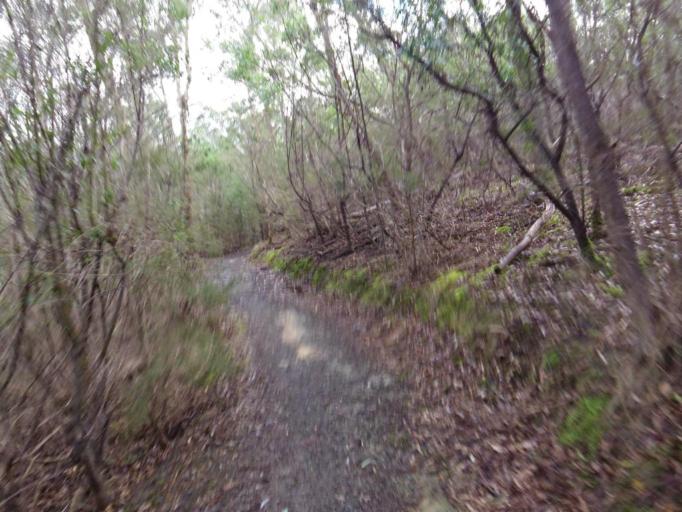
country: AU
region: Victoria
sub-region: Manningham
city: Donvale
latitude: -37.7571
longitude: 145.1824
